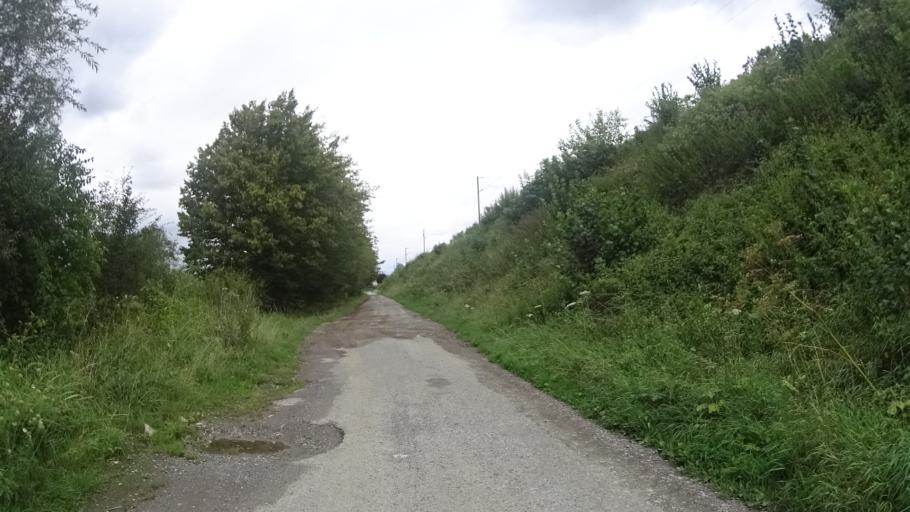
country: FR
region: Nord-Pas-de-Calais
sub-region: Departement du Nord
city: Bachant
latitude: 50.2359
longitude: 3.8930
